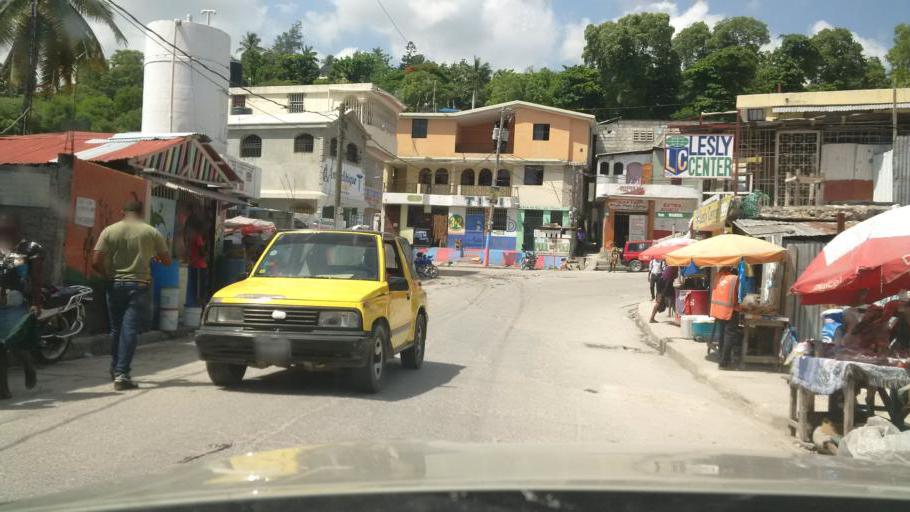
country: HT
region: Ouest
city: Delmas 73
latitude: 18.5413
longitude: -72.3173
